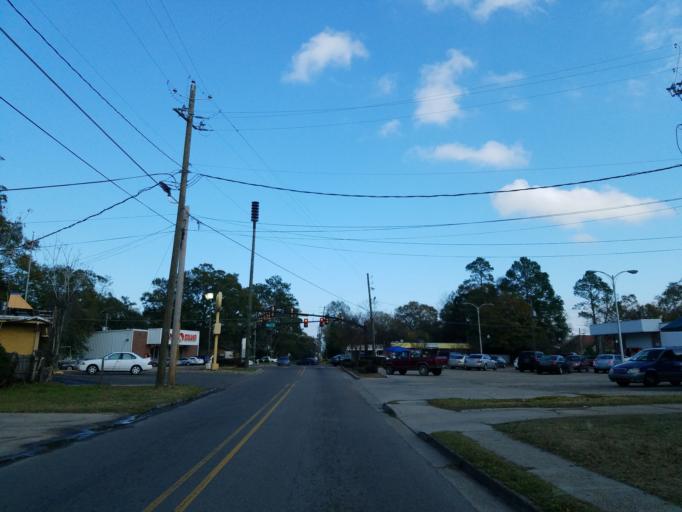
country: US
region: Mississippi
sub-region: Forrest County
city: Hattiesburg
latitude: 31.3357
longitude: -89.2999
